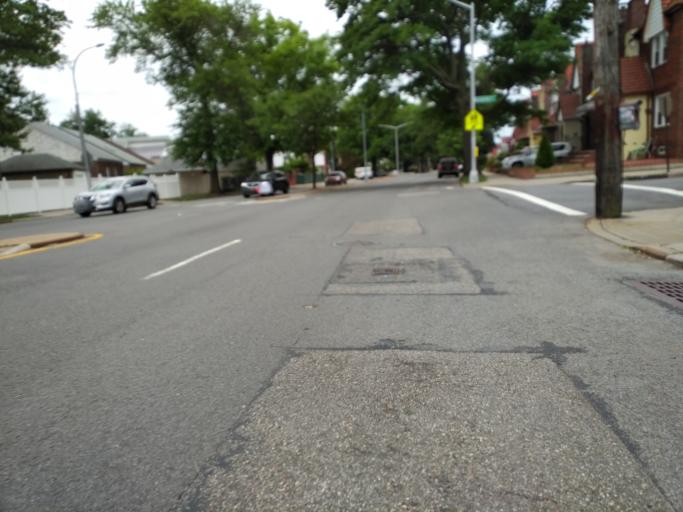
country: US
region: New York
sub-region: Nassau County
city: East Atlantic Beach
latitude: 40.7513
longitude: -73.7922
